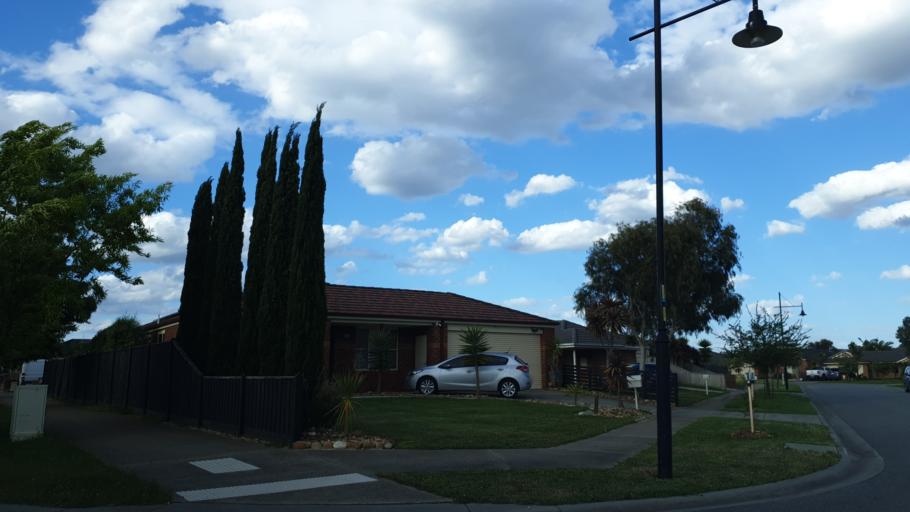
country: AU
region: Victoria
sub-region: Casey
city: Cranbourne North
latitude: -38.0858
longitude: 145.2876
